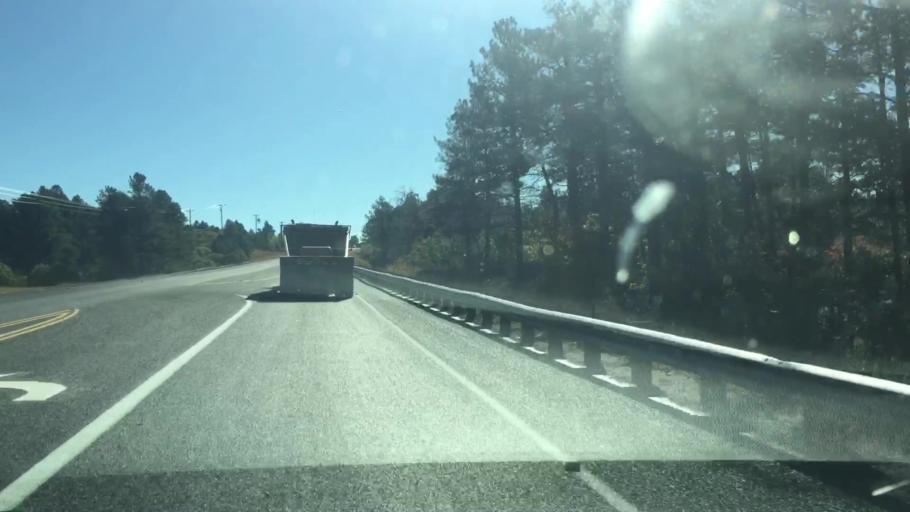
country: US
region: Colorado
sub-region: Elbert County
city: Ponderosa Park
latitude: 39.3765
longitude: -104.6939
